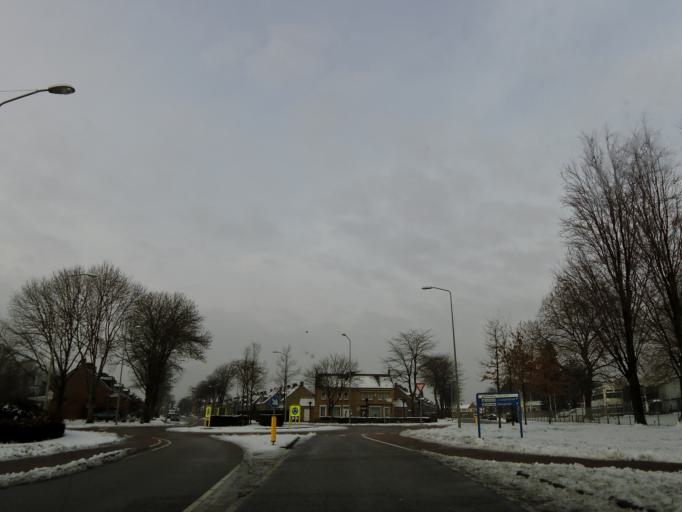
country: NL
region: Limburg
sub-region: Gemeente Heerlen
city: Heerlen
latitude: 50.8808
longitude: 6.0055
